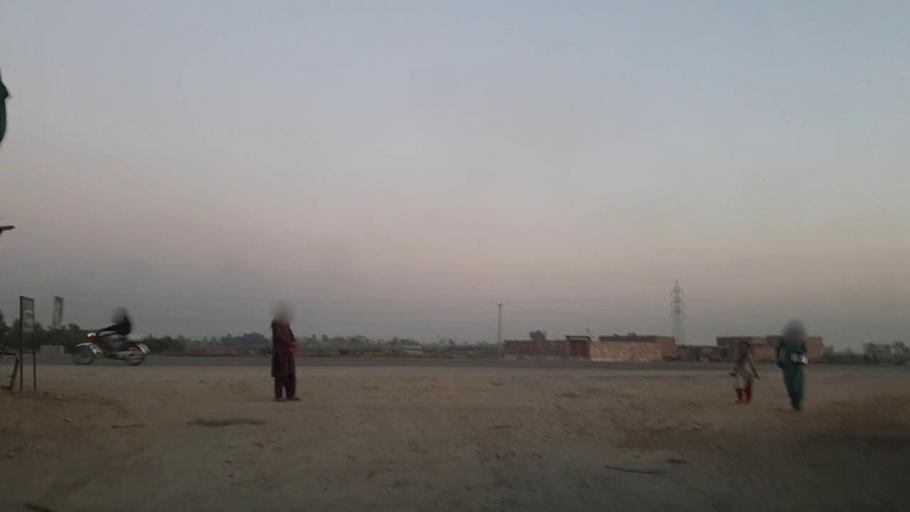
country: PK
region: Sindh
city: Naushahro Firoz
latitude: 26.7739
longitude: 68.0849
